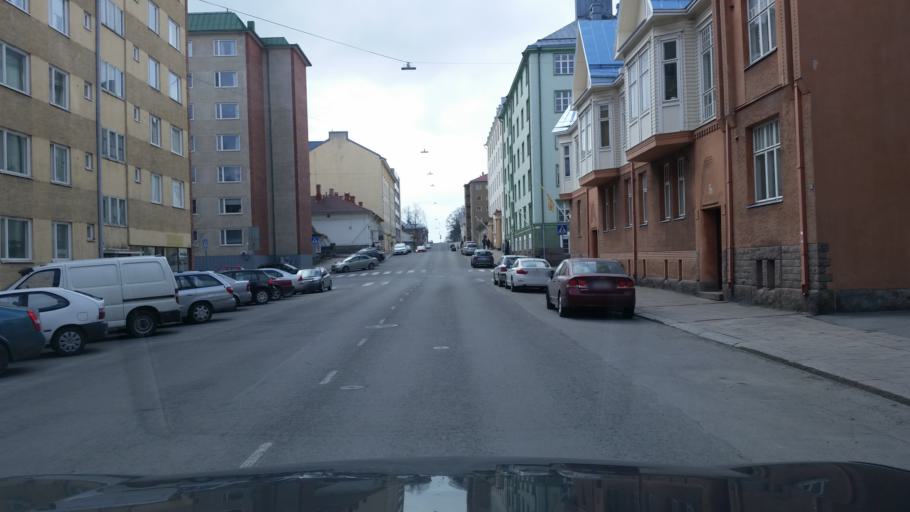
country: FI
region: Varsinais-Suomi
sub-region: Turku
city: Turku
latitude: 60.4485
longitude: 22.2853
